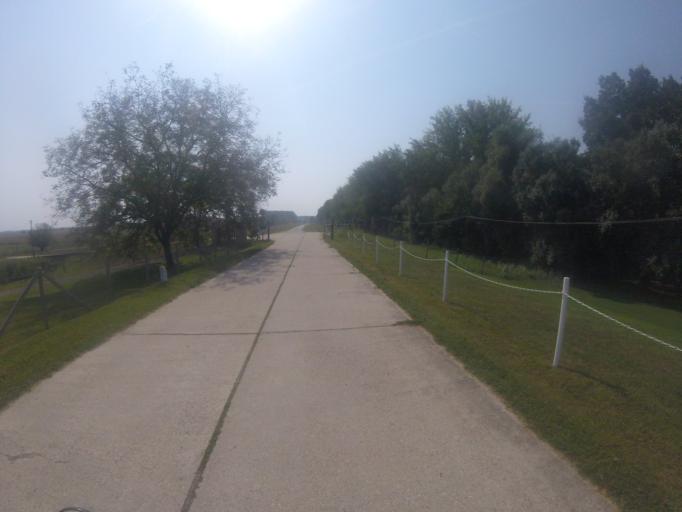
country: HU
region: Bacs-Kiskun
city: Ersekcsanad
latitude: 46.2516
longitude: 18.9177
